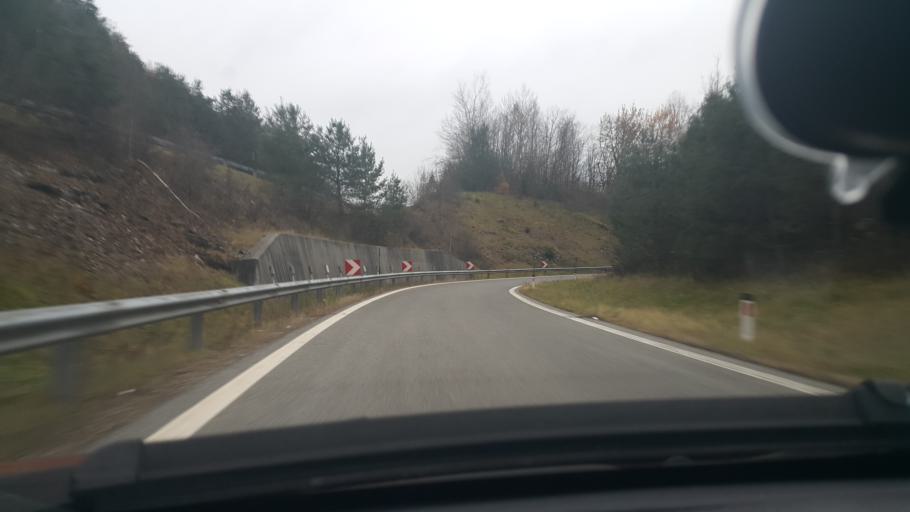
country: AT
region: Carinthia
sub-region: Politischer Bezirk Klagenfurt Land
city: Keutschach am See
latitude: 46.6311
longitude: 14.2409
